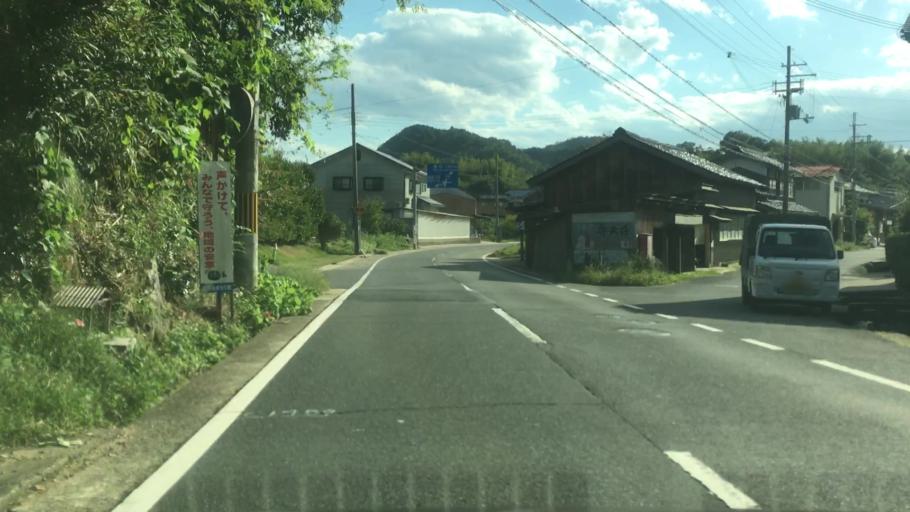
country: JP
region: Hyogo
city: Toyooka
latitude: 35.6373
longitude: 134.9421
